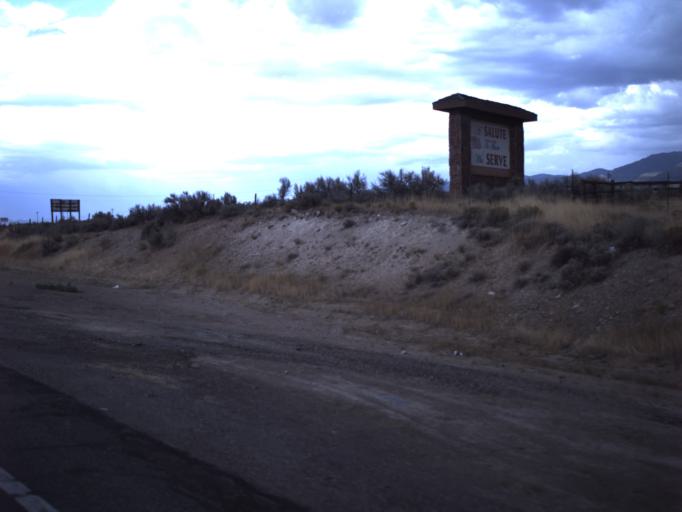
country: US
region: Utah
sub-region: Millard County
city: Fillmore
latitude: 38.9864
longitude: -112.3237
